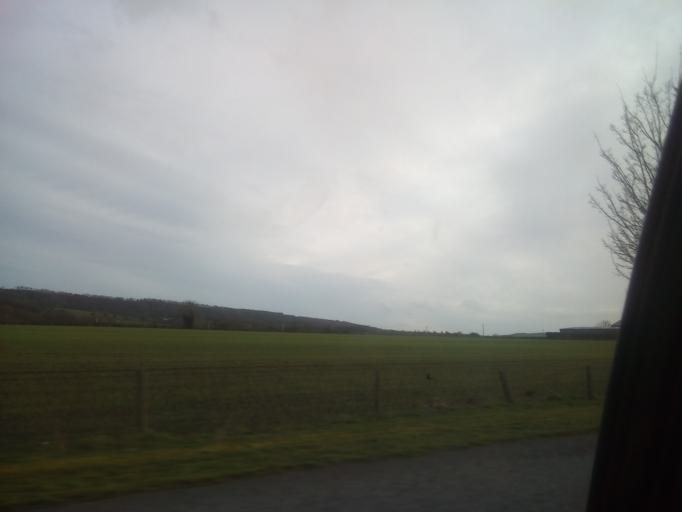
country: IE
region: Leinster
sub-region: Laois
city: Abbeyleix
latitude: 52.8401
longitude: -7.4094
